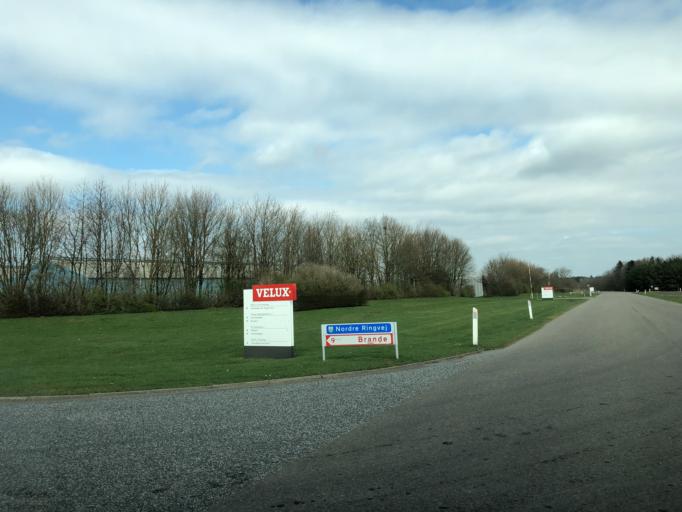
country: DK
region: South Denmark
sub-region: Vejle Kommune
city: Give
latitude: 55.9121
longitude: 9.2656
